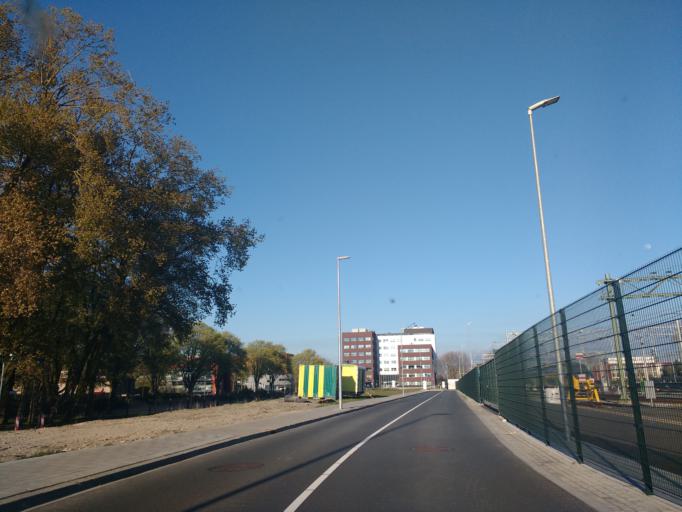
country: NL
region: North Holland
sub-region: Gemeente Alkmaar
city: Alkmaar
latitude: 52.6386
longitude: 4.7411
